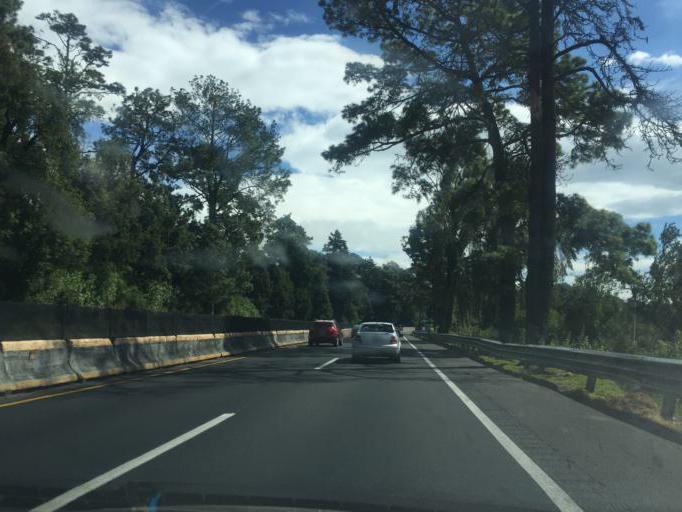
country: MX
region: Morelos
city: Tres Marias
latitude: 19.0310
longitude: -99.2182
